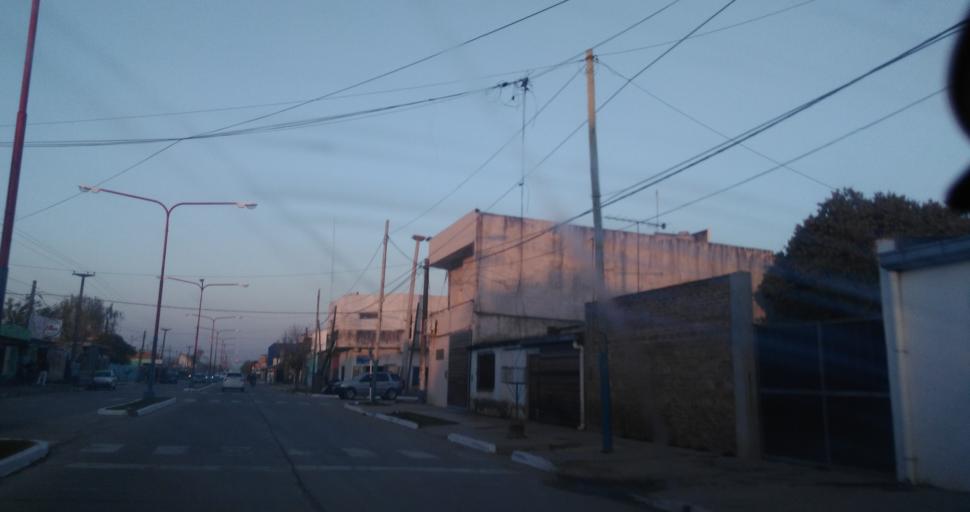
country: AR
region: Chaco
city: Resistencia
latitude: -27.4811
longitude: -58.9772
